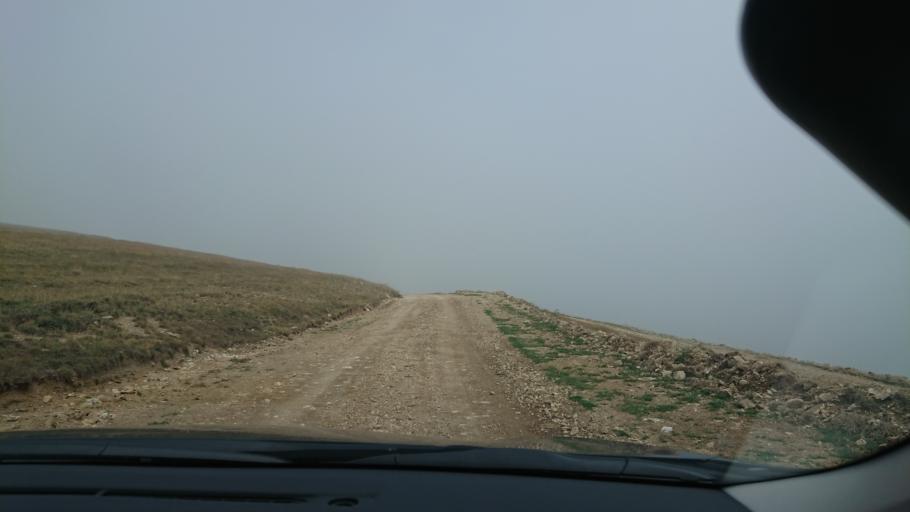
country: TR
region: Gumushane
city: Kurtun
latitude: 40.6280
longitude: 38.9958
